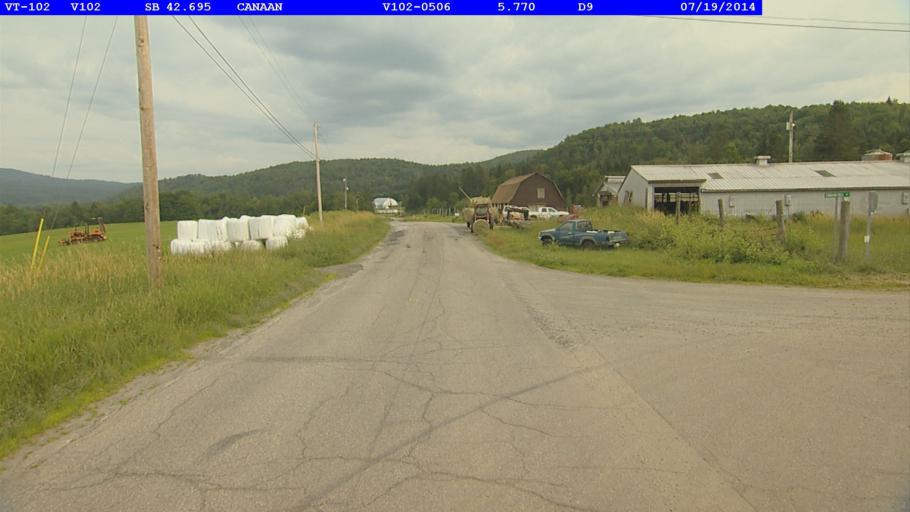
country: US
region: New Hampshire
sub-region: Coos County
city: Colebrook
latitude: 44.9820
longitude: -71.5432
